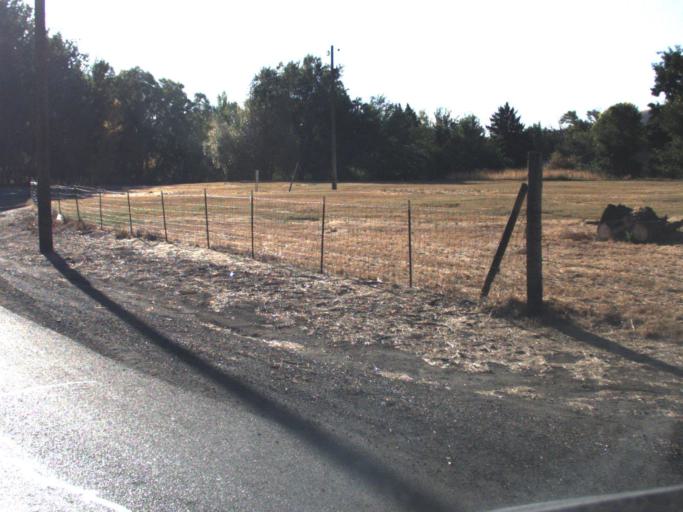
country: US
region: Washington
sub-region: Benton County
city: Benton City
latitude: 46.2575
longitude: -119.4769
